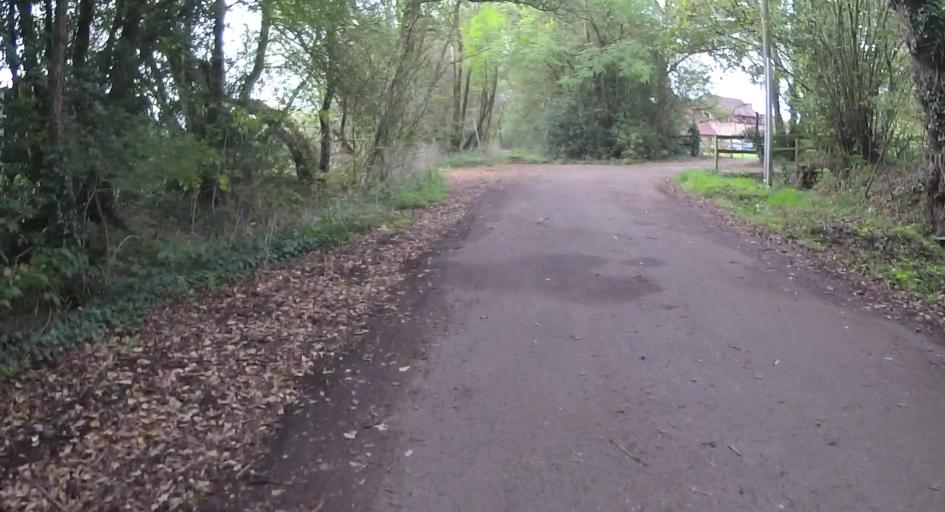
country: GB
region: England
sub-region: Hampshire
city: Eversley
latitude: 51.3630
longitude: -0.9146
